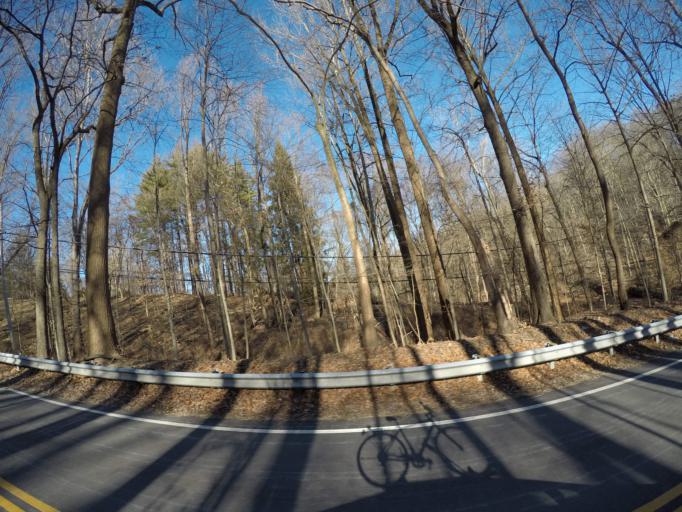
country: US
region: Maryland
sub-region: Howard County
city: Ilchester
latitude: 39.2520
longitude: -76.7795
